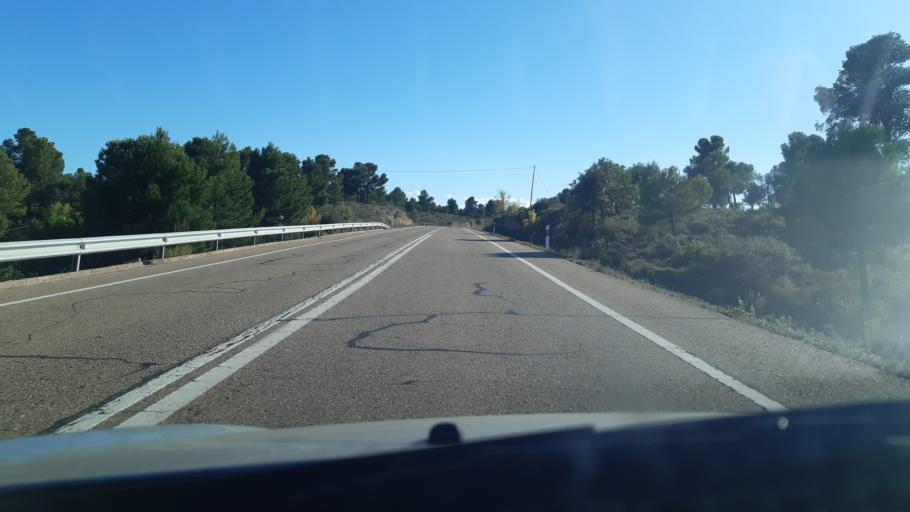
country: ES
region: Aragon
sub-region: Provincia de Teruel
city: Fornoles
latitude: 40.9326
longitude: -0.0124
